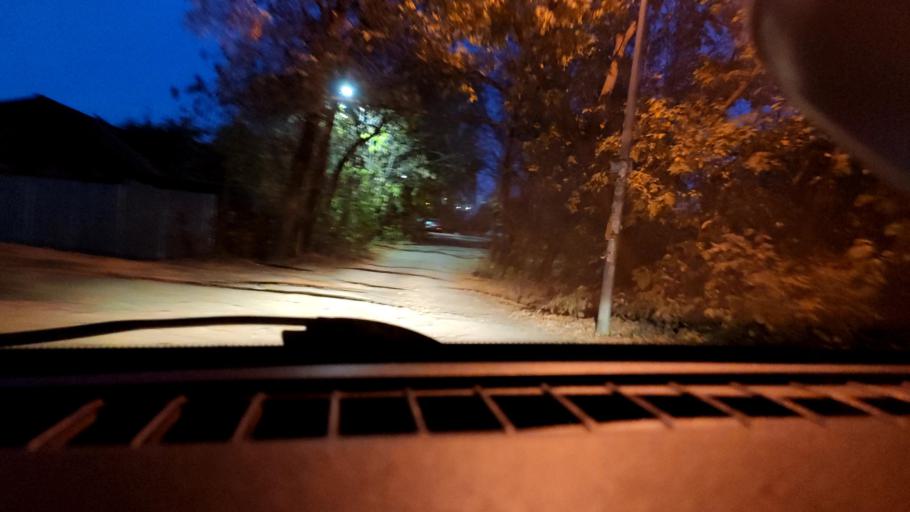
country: RU
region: Samara
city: Samara
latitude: 53.2162
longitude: 50.2154
